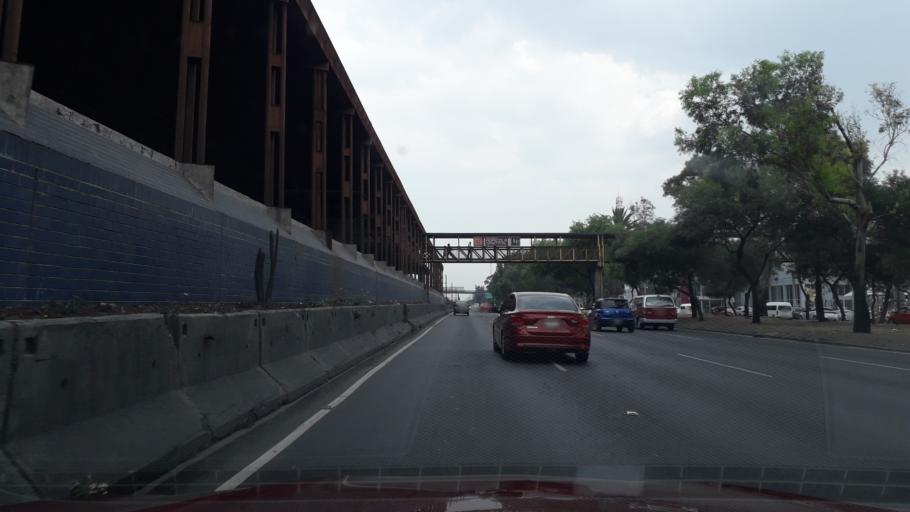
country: MX
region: Mexico City
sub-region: Iztacalco
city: Iztacalco
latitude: 19.4049
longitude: -99.0702
